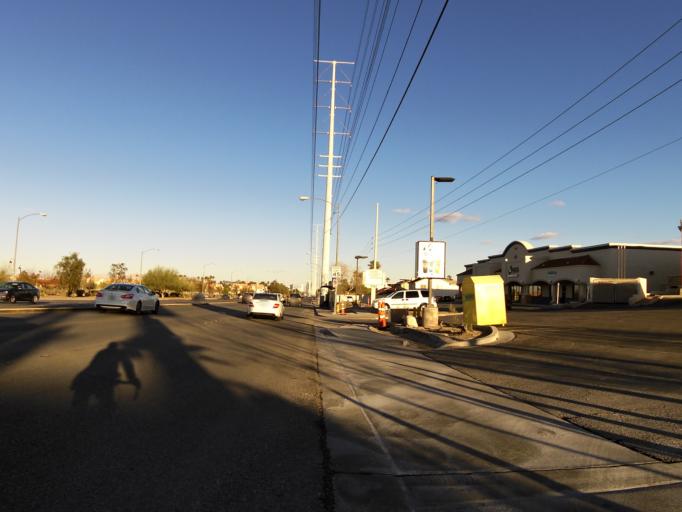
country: US
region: Nevada
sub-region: Clark County
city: Spring Valley
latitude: 36.1146
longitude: -115.2607
